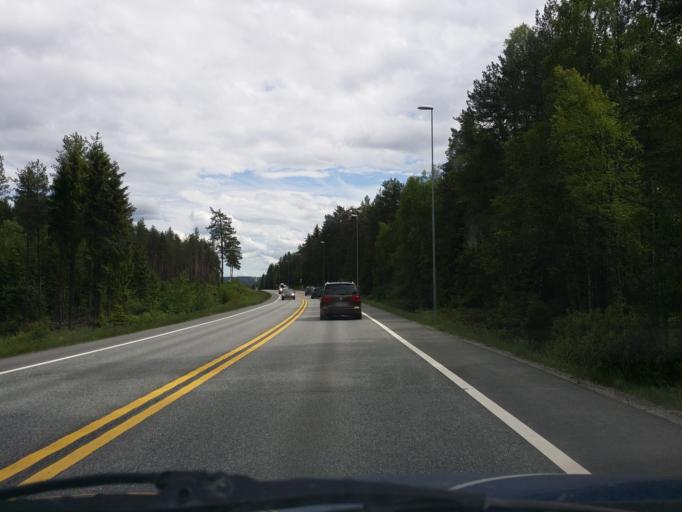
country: NO
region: Hedmark
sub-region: Stange
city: Stange
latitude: 60.7103
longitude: 11.2533
